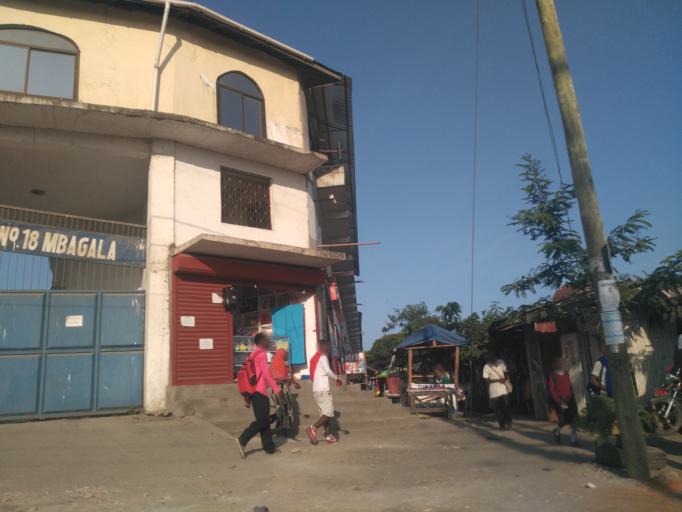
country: TZ
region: Pwani
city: Vikindu
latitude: -6.9194
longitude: 39.2683
